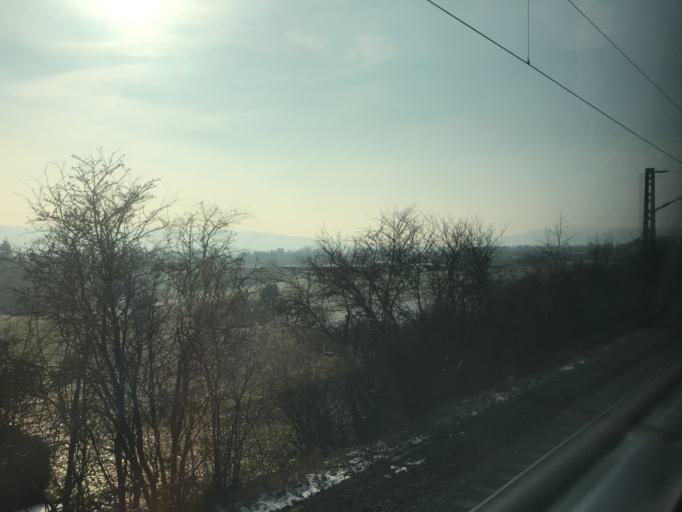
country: DE
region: Rheinland-Pfalz
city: Schweich
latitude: 49.8304
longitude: 6.7374
